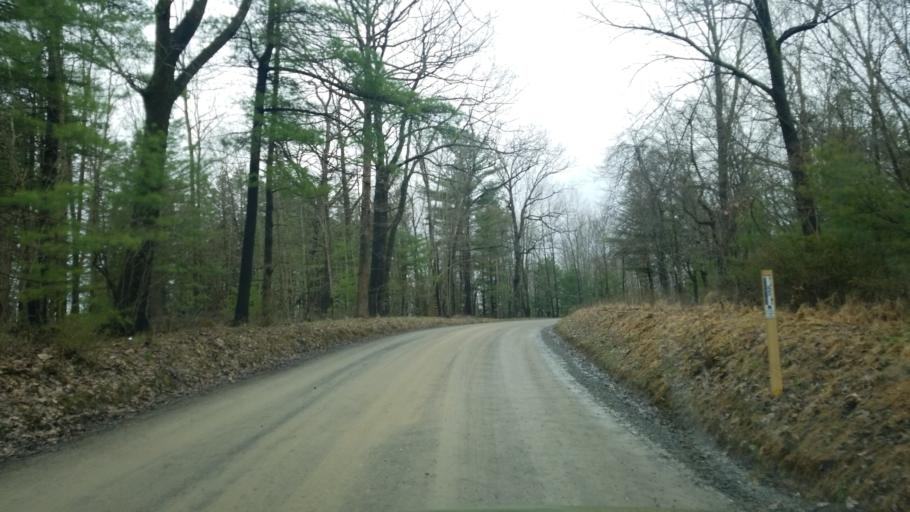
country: US
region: Pennsylvania
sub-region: Clearfield County
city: Shiloh
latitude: 41.1430
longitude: -78.3368
